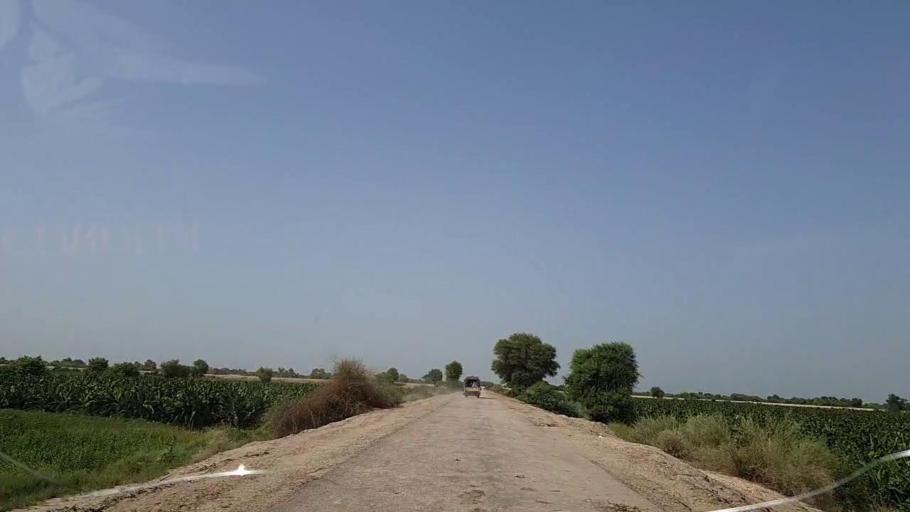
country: PK
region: Sindh
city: Kandiaro
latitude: 27.0524
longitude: 68.1347
